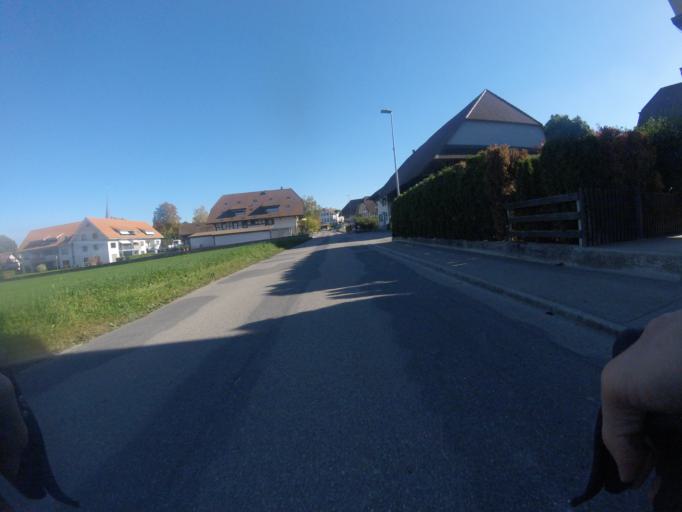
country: CH
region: Bern
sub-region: Seeland District
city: Schupfen
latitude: 47.0384
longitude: 7.3741
